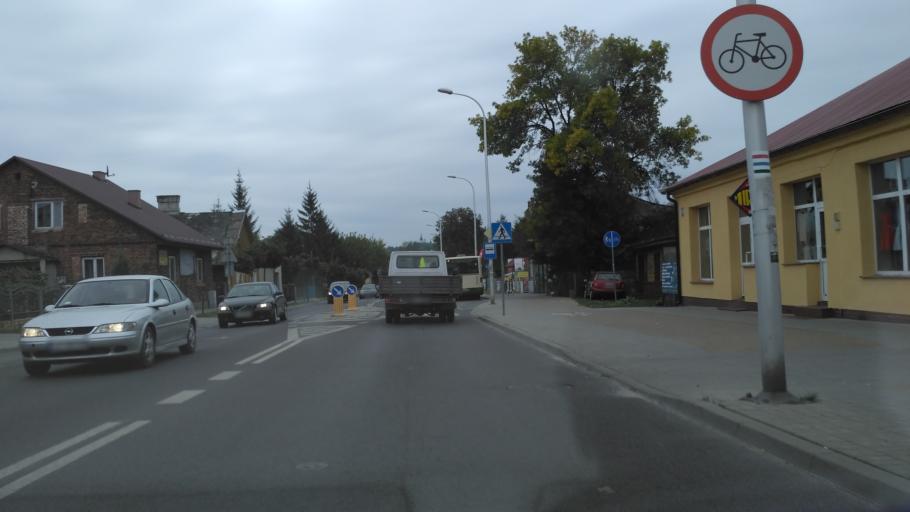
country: PL
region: Lublin Voivodeship
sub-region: Chelm
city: Chelm
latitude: 51.1395
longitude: 23.4564
